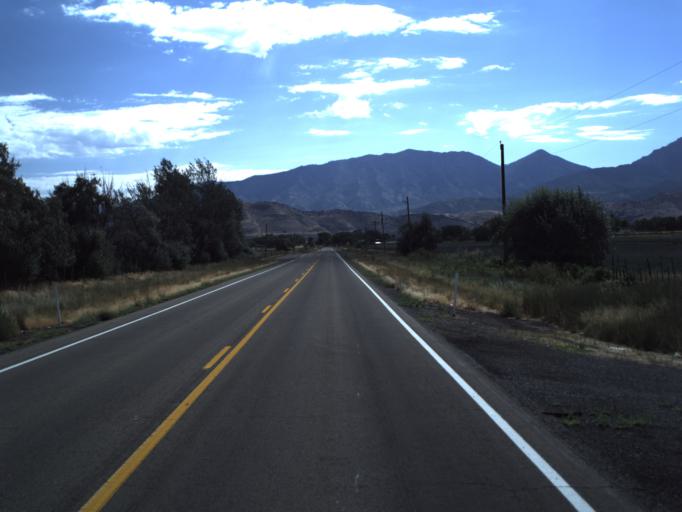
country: US
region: Utah
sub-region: Utah County
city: Genola
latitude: 39.9524
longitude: -111.9188
